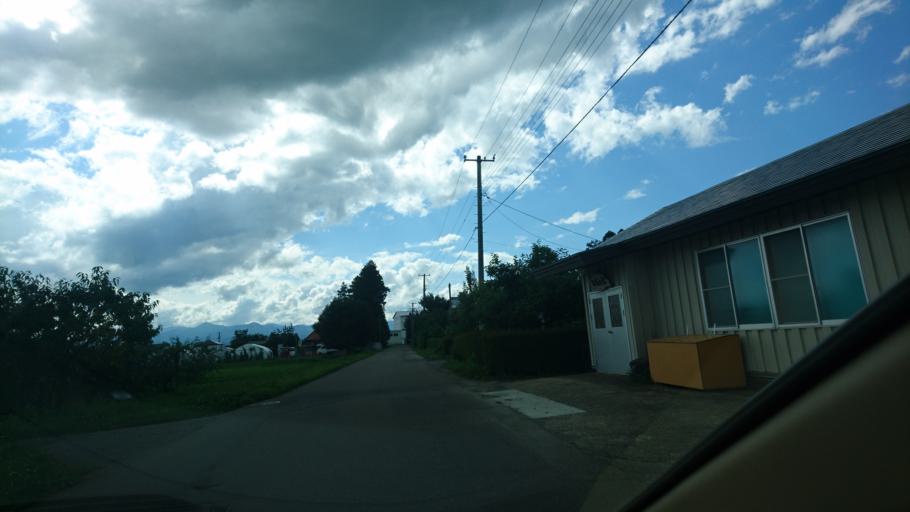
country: JP
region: Iwate
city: Mizusawa
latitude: 39.1947
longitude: 141.1516
